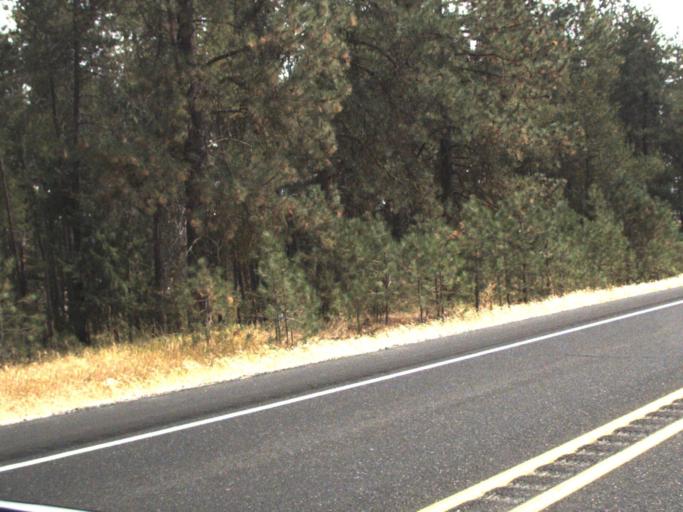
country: US
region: Washington
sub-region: Spokane County
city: Deer Park
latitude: 47.9568
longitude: -117.4909
